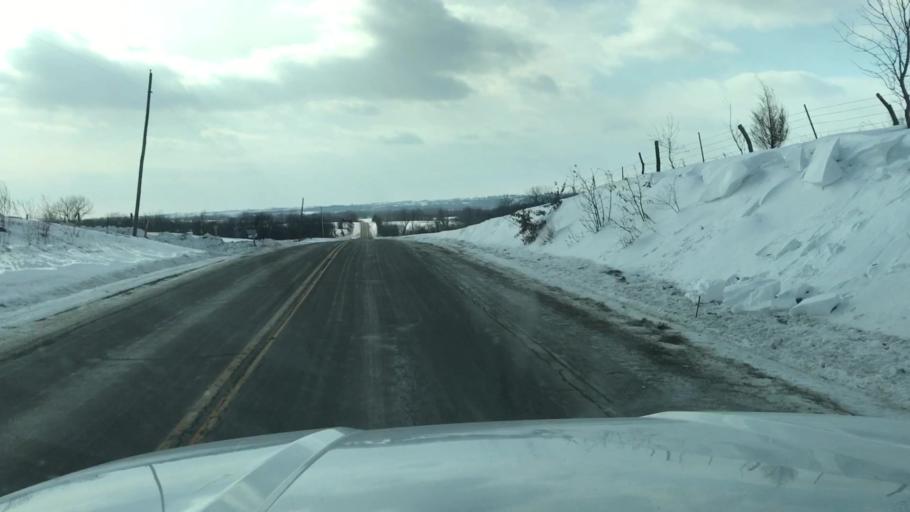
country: US
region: Missouri
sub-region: Gentry County
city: Stanberry
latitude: 40.3659
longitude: -94.6513
